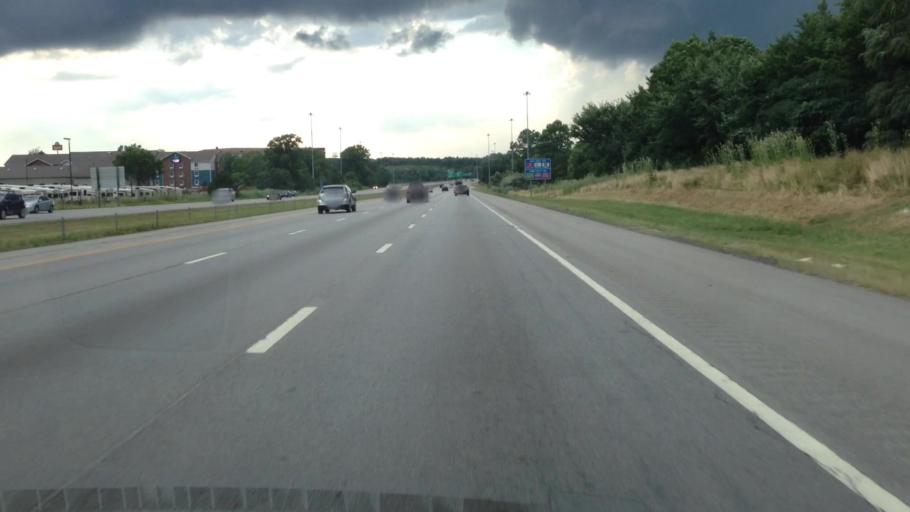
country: US
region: Ohio
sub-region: Summit County
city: Green
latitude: 40.9800
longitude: -81.4842
